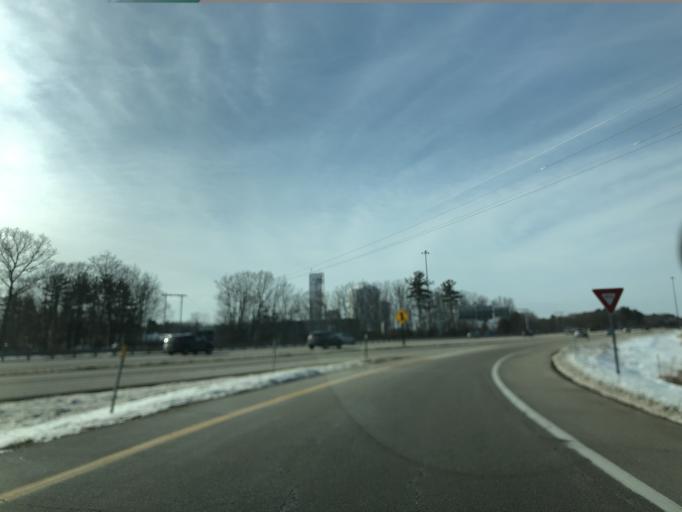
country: US
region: Maine
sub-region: York County
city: Kittery
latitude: 43.1033
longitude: -70.7501
